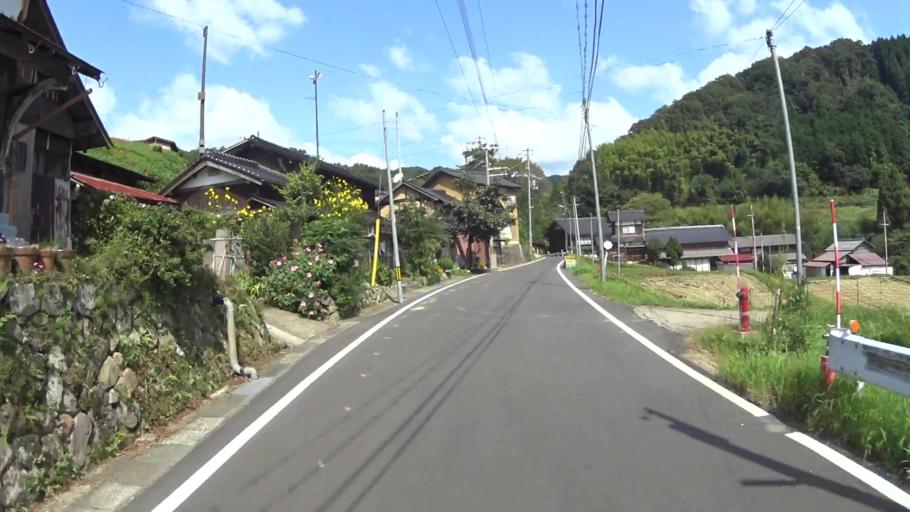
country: JP
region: Kyoto
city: Miyazu
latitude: 35.6322
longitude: 135.2313
